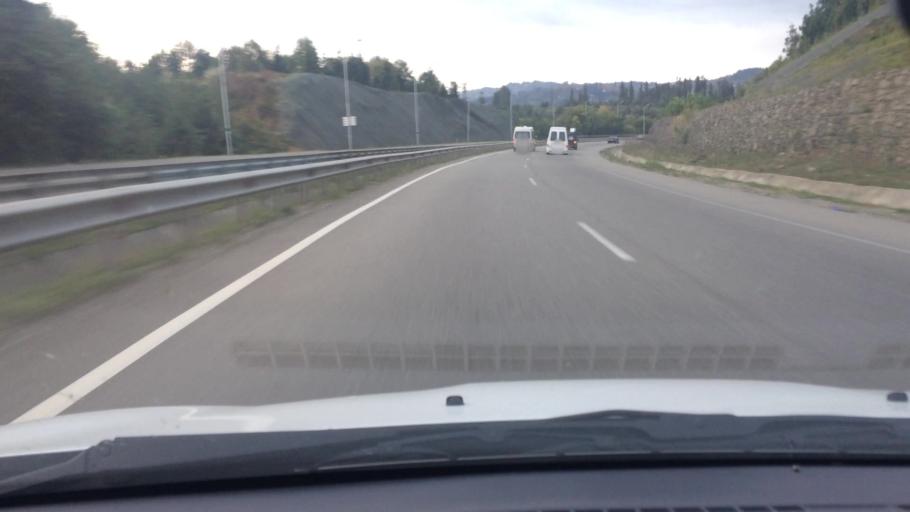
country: GE
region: Ajaria
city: Makhinjauri
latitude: 41.6978
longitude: 41.7279
